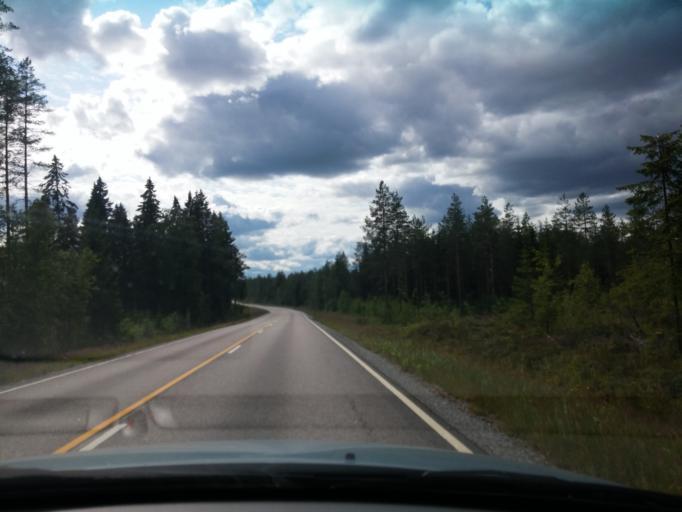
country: FI
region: Central Finland
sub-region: Saarijaervi-Viitasaari
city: Pylkoenmaeki
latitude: 62.6103
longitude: 24.6888
